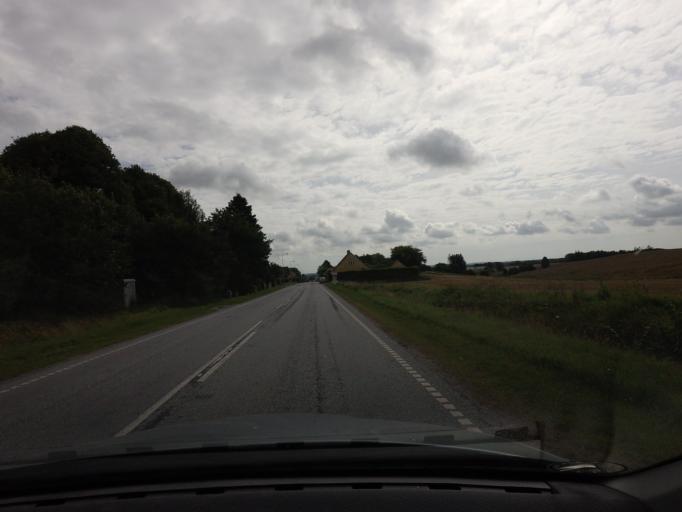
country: DK
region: North Denmark
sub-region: Bronderslev Kommune
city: Dronninglund
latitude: 57.2839
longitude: 10.2285
